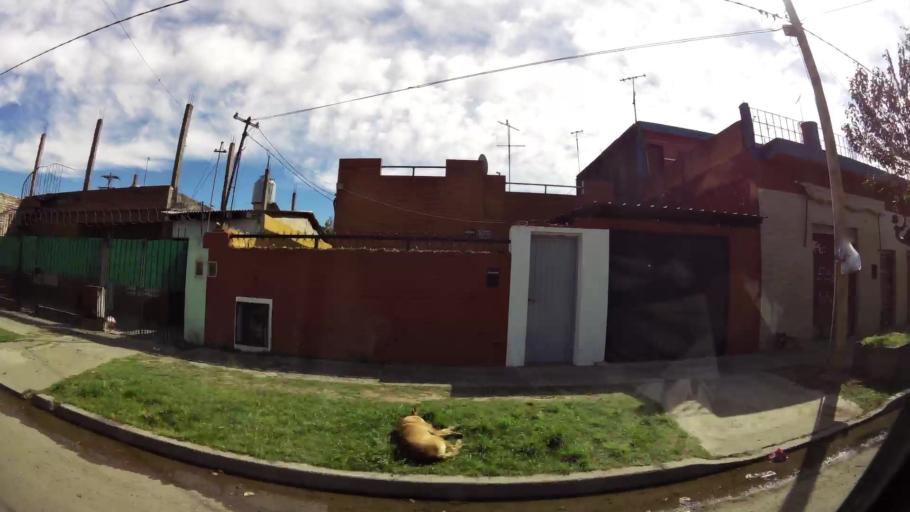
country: AR
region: Buenos Aires
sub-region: Partido de Quilmes
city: Quilmes
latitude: -34.7766
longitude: -58.3026
